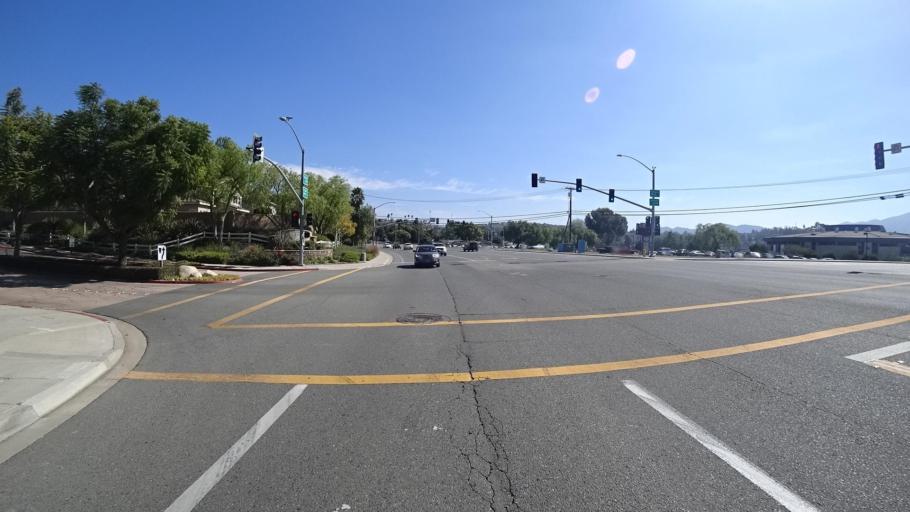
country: US
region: California
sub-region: San Diego County
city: Rancho San Diego
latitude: 32.7627
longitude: -116.9211
